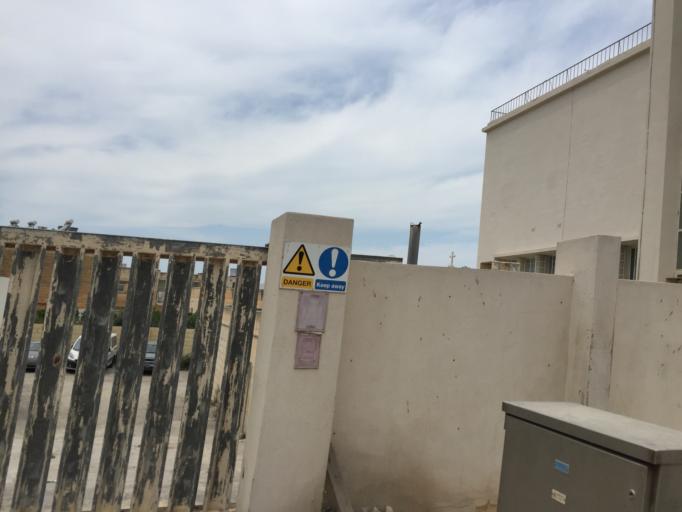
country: MT
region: Tal-Pieta
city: Pieta
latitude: 35.8916
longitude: 14.4926
